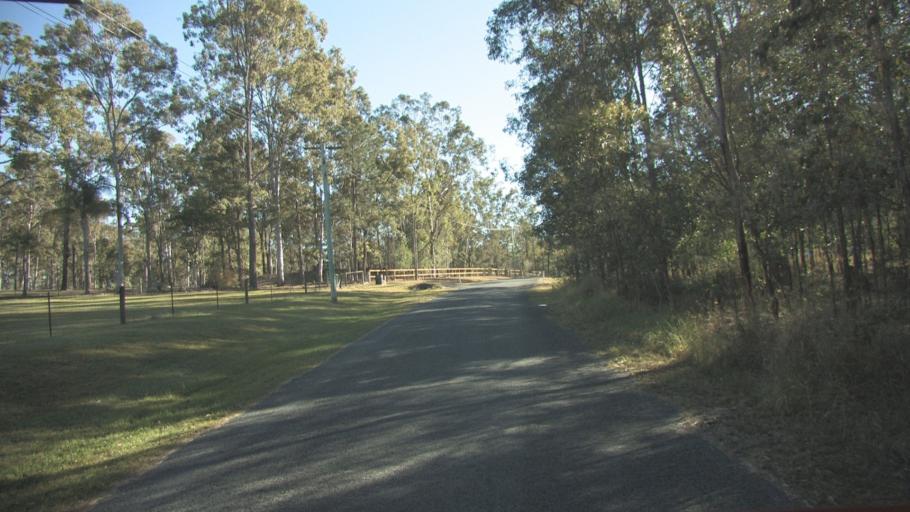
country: AU
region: Queensland
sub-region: Logan
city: North Maclean
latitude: -27.7822
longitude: 152.9652
